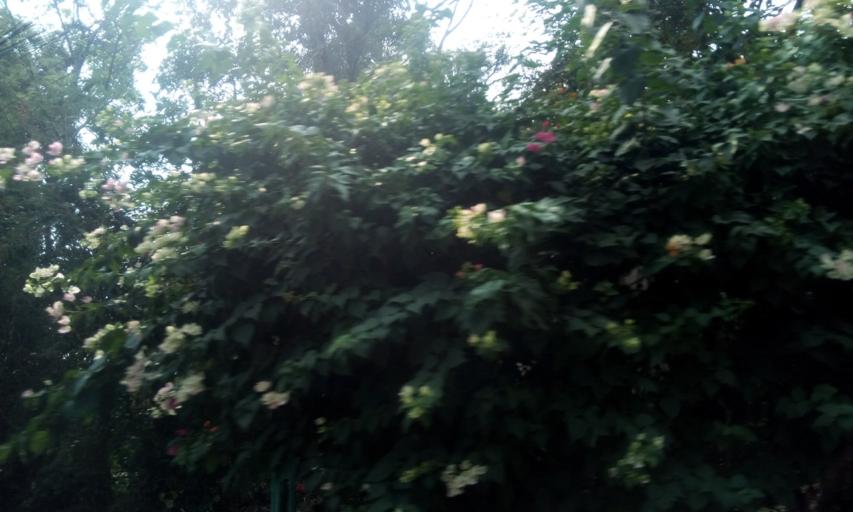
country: TH
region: Nakhon Nayok
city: Nakhon Nayok
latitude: 14.3235
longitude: 101.3040
